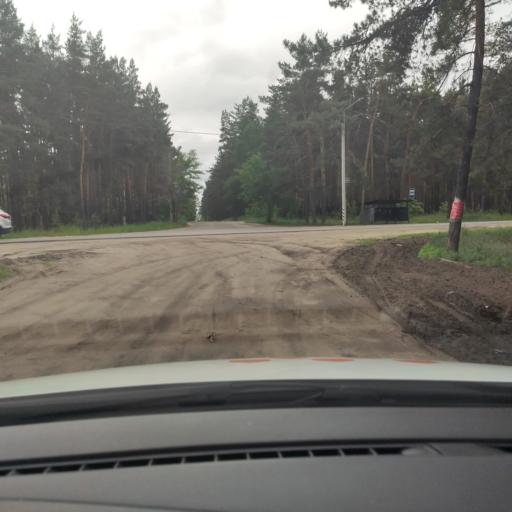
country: RU
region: Voronezj
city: Maslovka
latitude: 51.5500
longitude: 39.2215
